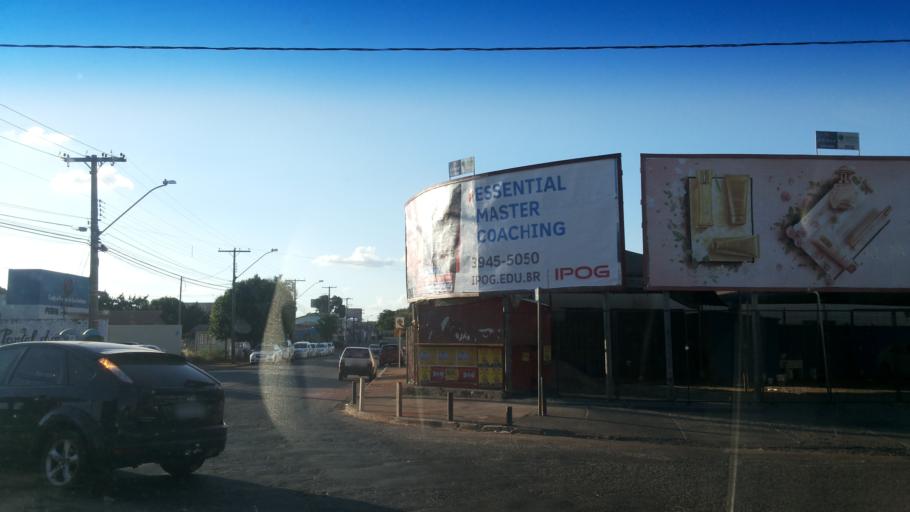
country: BR
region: Goias
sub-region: Goiania
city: Goiania
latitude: -16.7161
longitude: -49.3068
